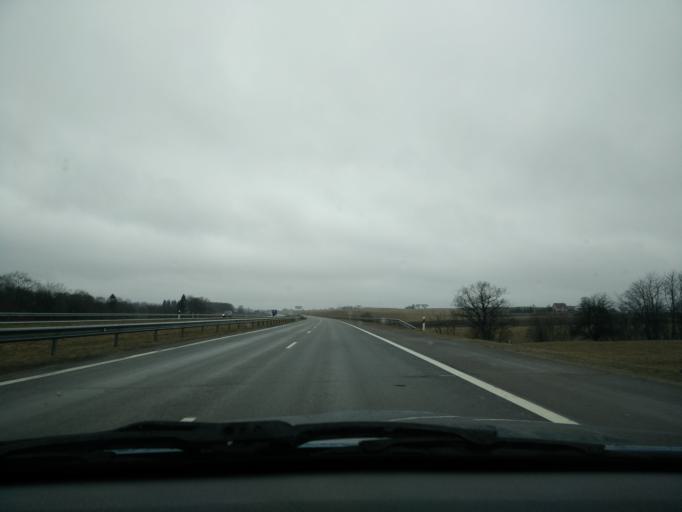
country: LT
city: Silale
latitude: 55.5255
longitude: 22.3591
